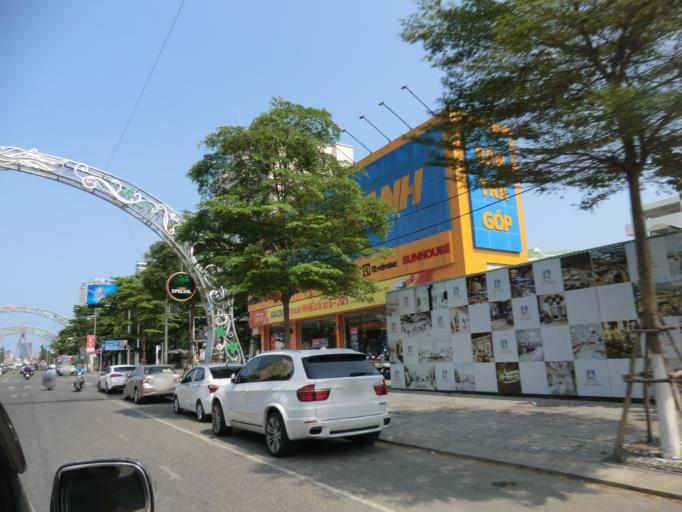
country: VN
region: Da Nang
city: Da Nang
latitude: 16.0718
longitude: 108.2223
